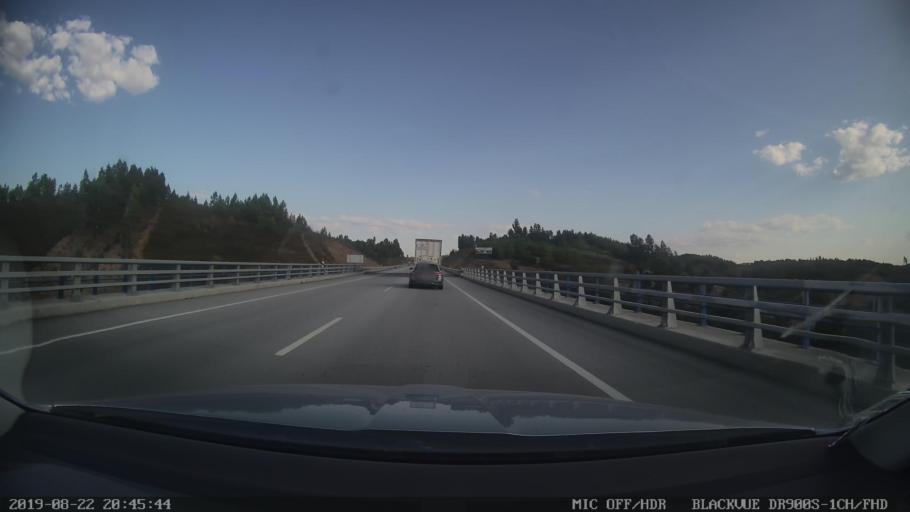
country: PT
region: Castelo Branco
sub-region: Proenca-A-Nova
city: Proenca-a-Nova
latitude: 39.7199
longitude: -7.8695
